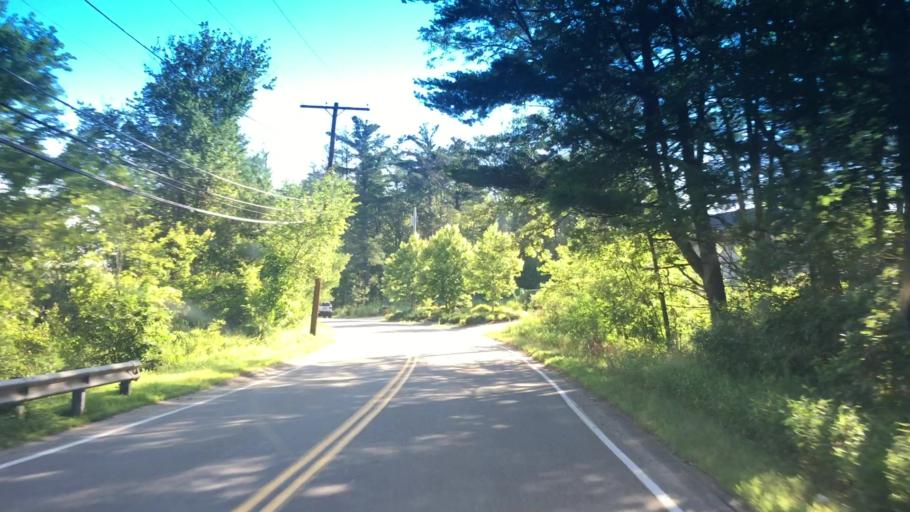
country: US
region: Massachusetts
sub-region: Norfolk County
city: Walpole
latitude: 42.1415
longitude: -71.2692
